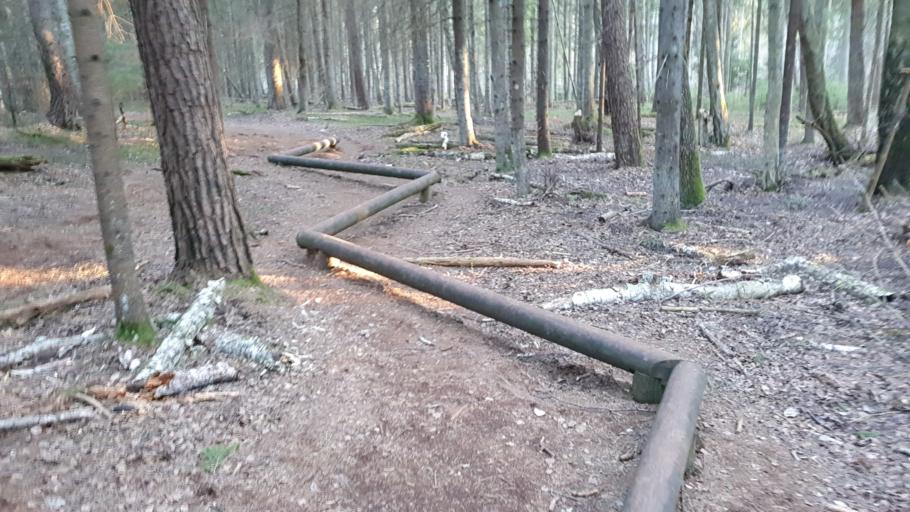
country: LV
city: Tireli
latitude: 56.9579
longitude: 23.5365
